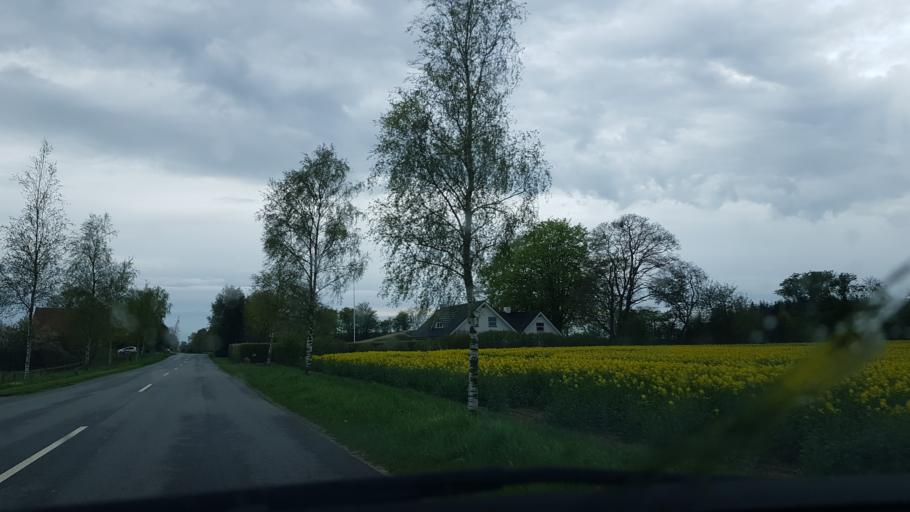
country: DK
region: South Denmark
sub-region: Kolding Kommune
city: Lunderskov
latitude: 55.4635
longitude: 9.3668
